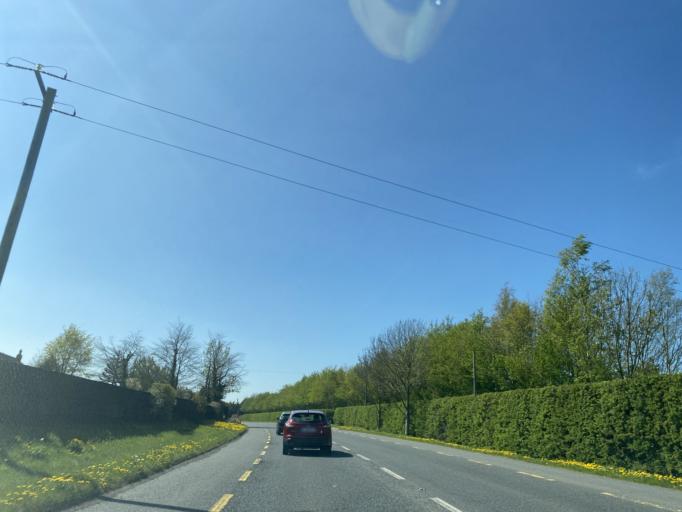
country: IE
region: Leinster
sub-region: Kildare
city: Maynooth
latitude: 53.3331
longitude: -6.6071
